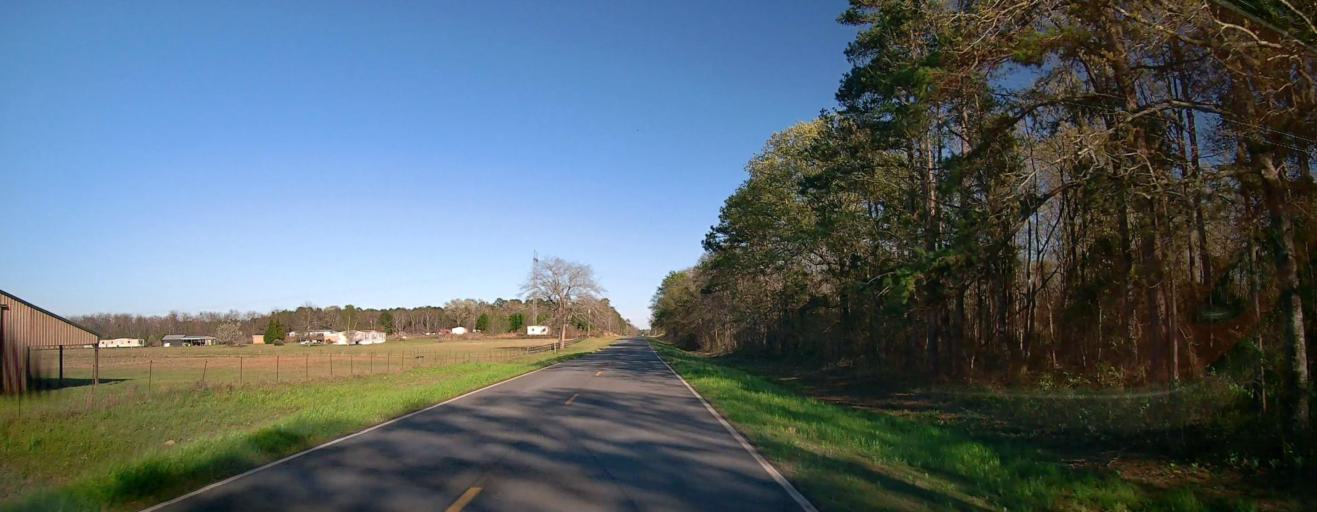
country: US
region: Georgia
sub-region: Pulaski County
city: Hawkinsville
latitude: 32.3477
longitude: -83.5911
